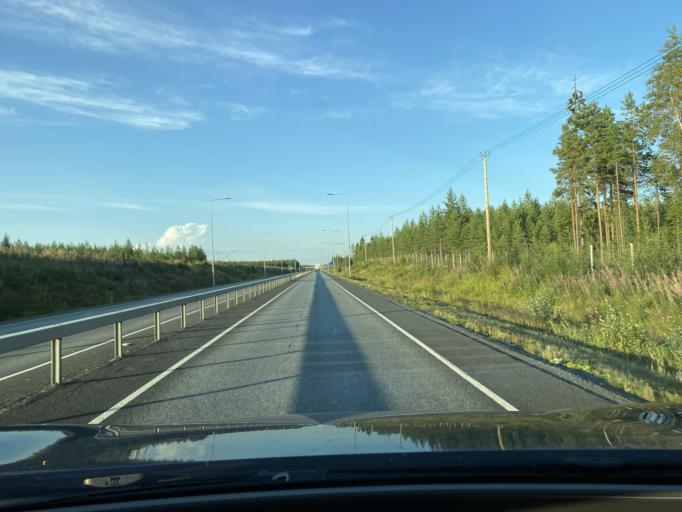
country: FI
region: Southern Ostrobothnia
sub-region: Seinaejoki
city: Seinaejoki
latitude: 62.7160
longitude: 22.8564
